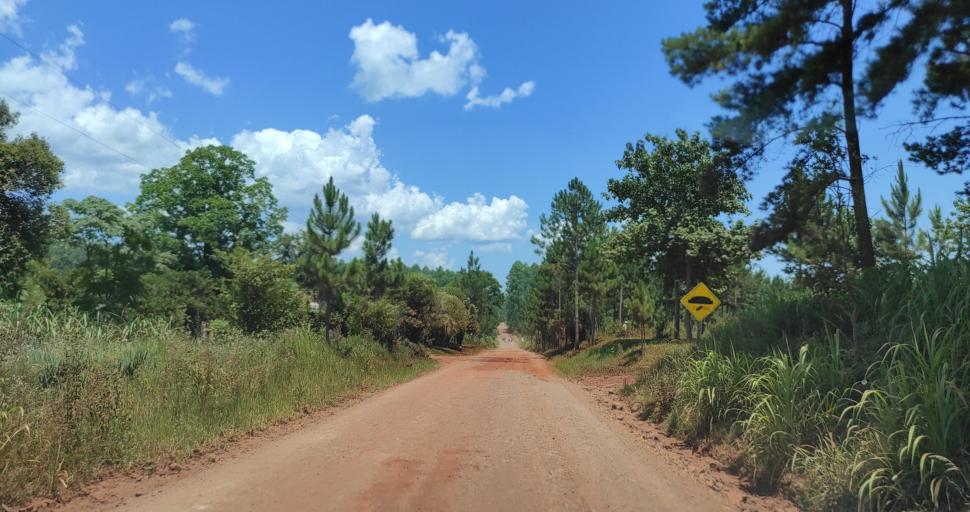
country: AR
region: Misiones
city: Ruiz de Montoya
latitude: -27.0425
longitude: -55.0207
